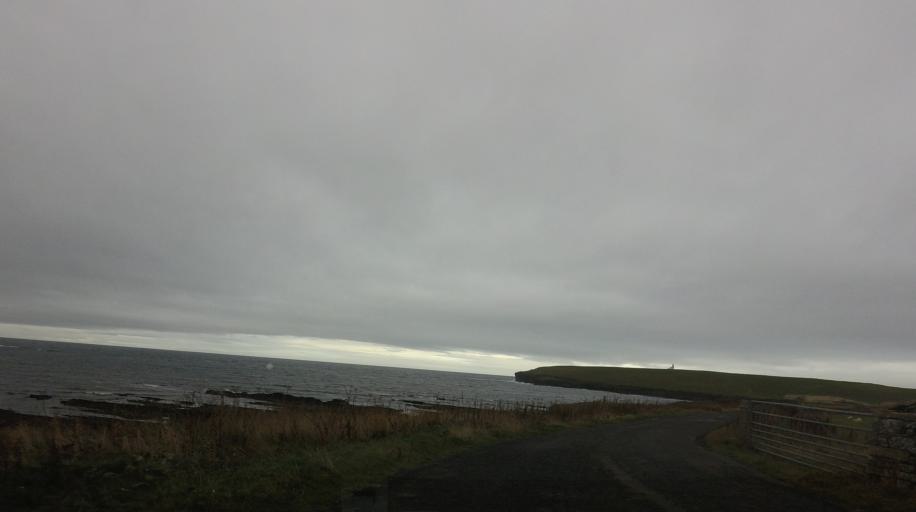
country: GB
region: Scotland
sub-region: Orkney Islands
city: Stromness
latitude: 59.1336
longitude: -3.3217
